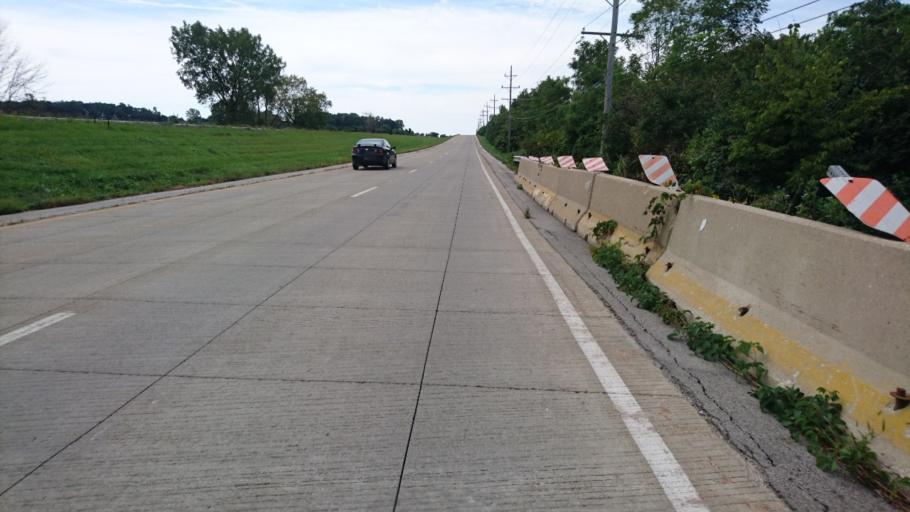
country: US
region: Illinois
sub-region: Will County
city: Elwood
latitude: 41.3849
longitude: -88.1228
